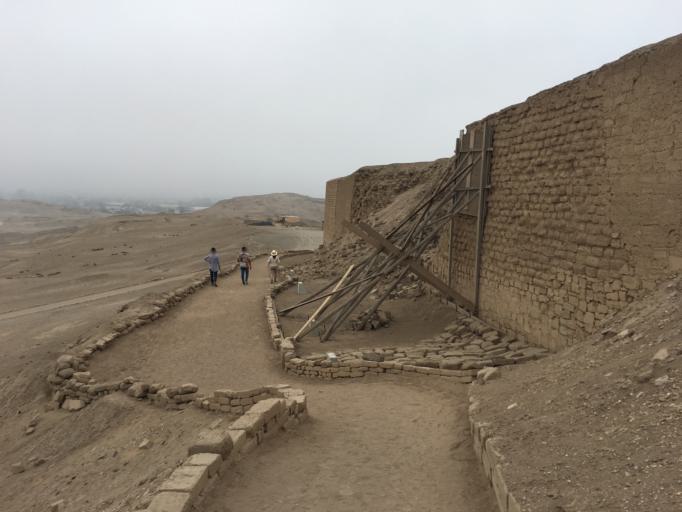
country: PE
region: Lima
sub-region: Lima
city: Punta Hermosa
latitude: -12.2621
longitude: -76.9020
